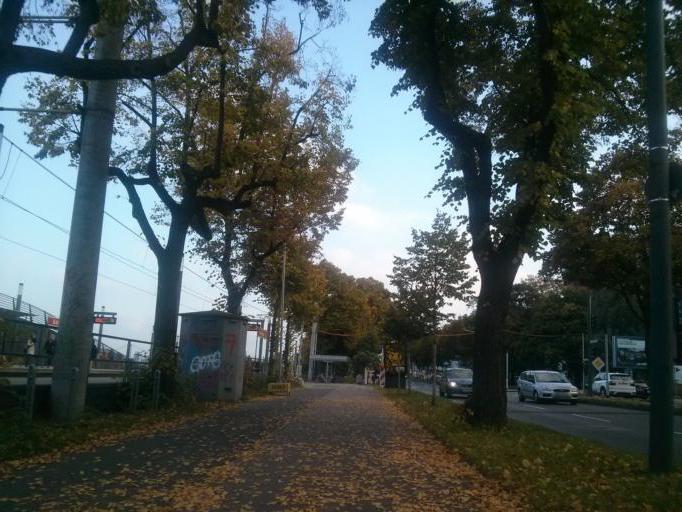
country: DE
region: North Rhine-Westphalia
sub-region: Regierungsbezirk Koln
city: Bayenthal
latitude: 50.9144
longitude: 6.9717
